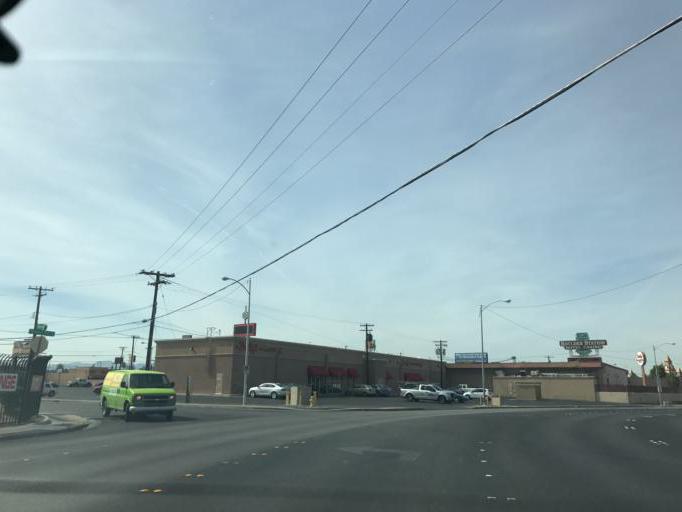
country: US
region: Nevada
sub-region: Clark County
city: Winchester
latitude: 36.1296
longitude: -115.0812
